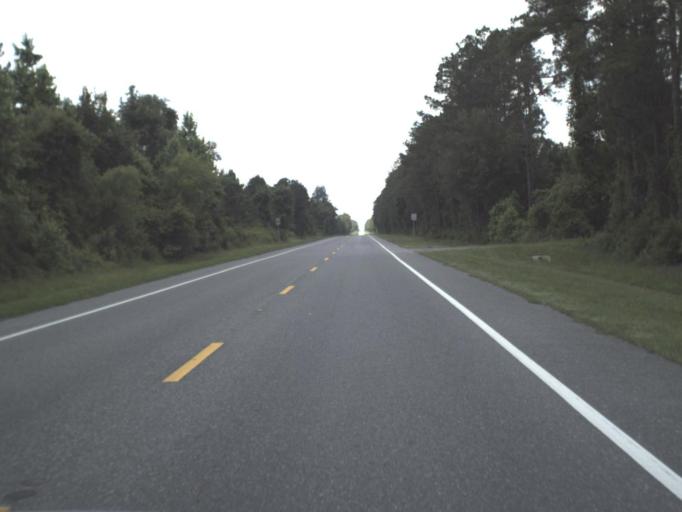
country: US
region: Florida
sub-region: Columbia County
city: Watertown
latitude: 30.1365
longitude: -82.5323
